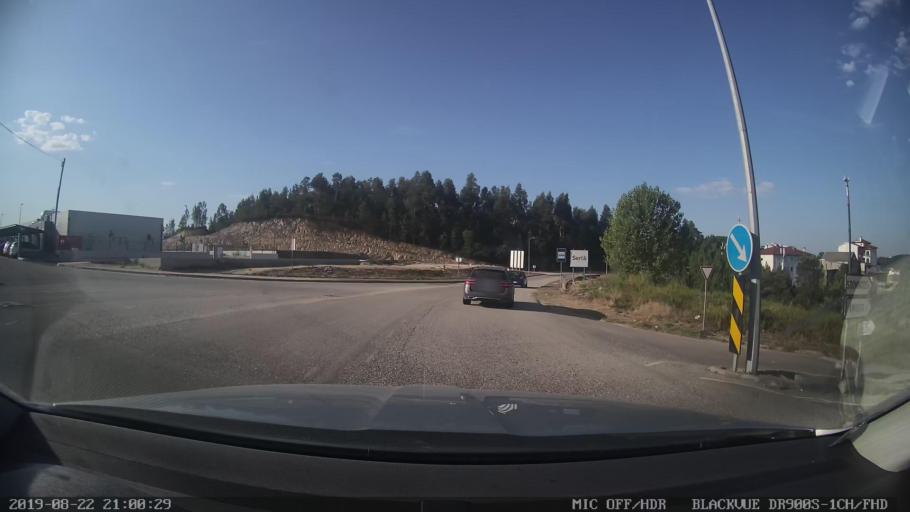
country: PT
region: Castelo Branco
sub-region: Serta
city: Serta
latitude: 39.8137
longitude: -8.0925
